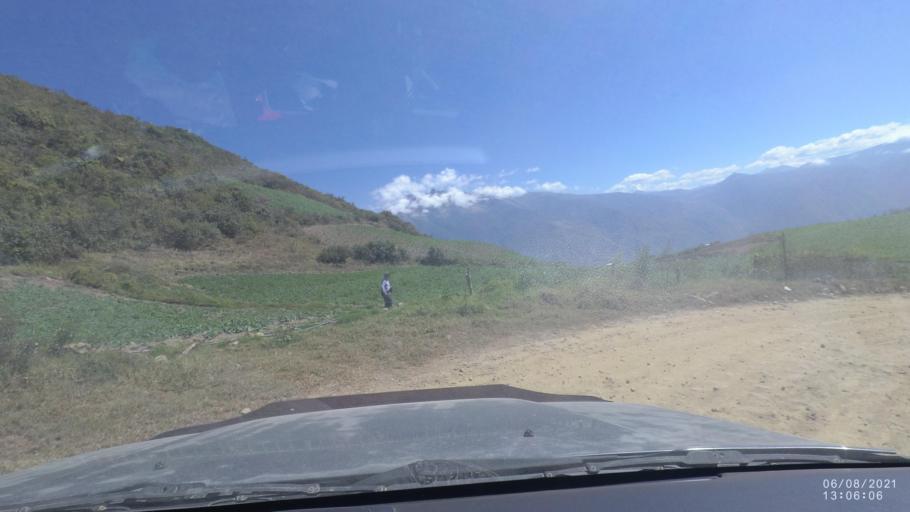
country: BO
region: La Paz
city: Quime
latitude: -16.7339
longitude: -66.7057
